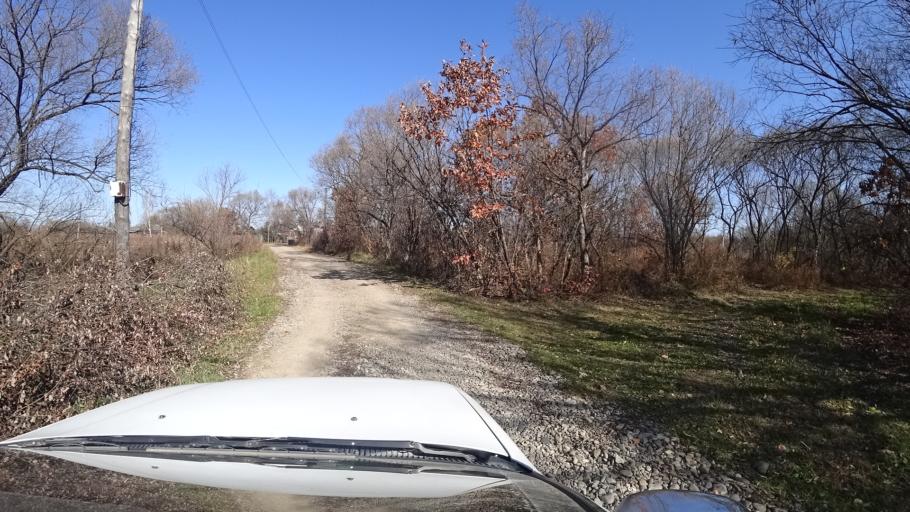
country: RU
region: Primorskiy
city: Dal'nerechensk
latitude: 45.9202
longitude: 133.7841
